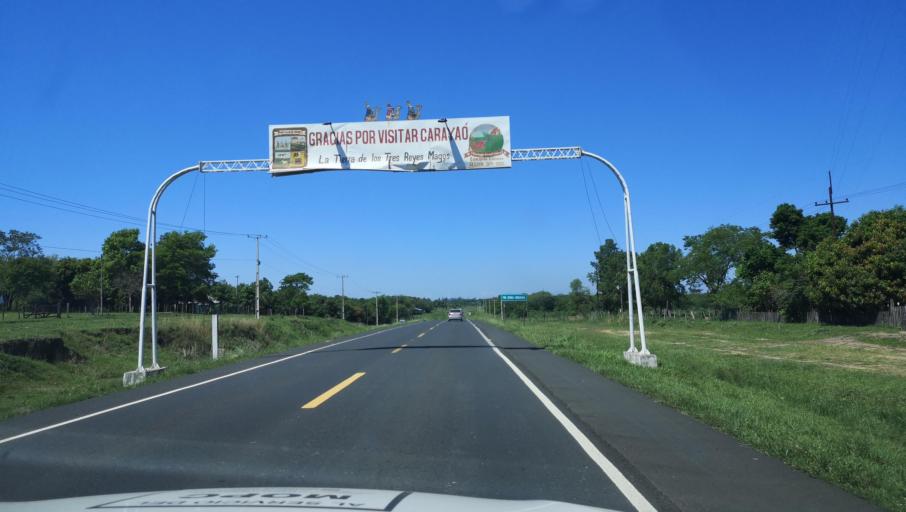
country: PY
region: Caaguazu
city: Carayao
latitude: -25.2092
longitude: -56.3984
